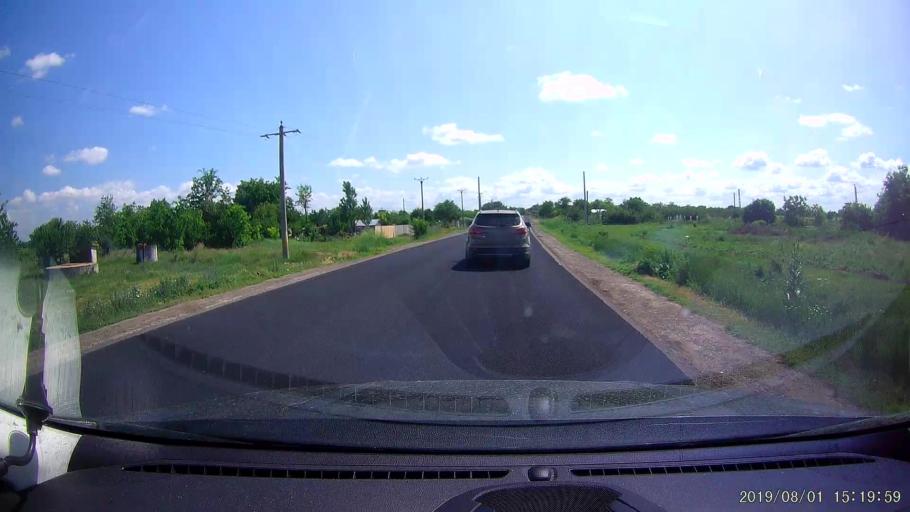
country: RO
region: Braila
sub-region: Comuna Tufesti
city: Tufesti
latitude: 45.0833
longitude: 27.8096
